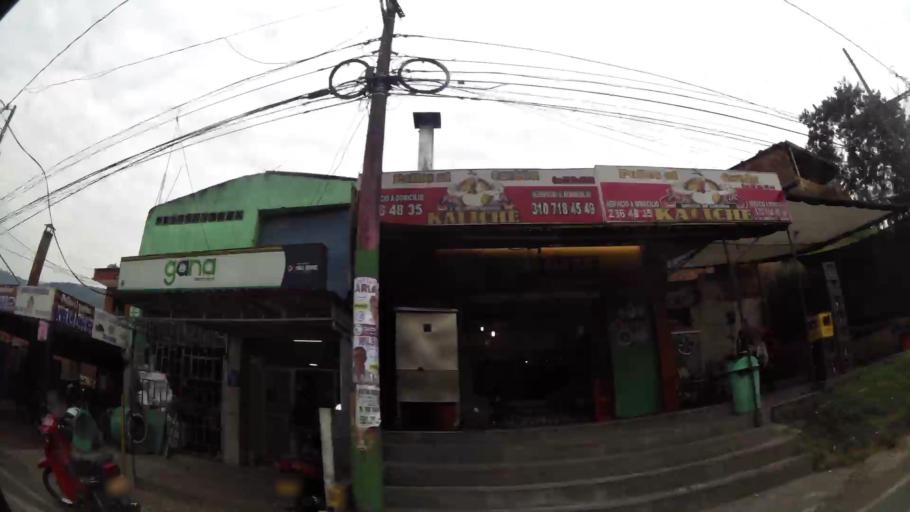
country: CO
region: Antioquia
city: Medellin
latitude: 6.2919
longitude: -75.5623
